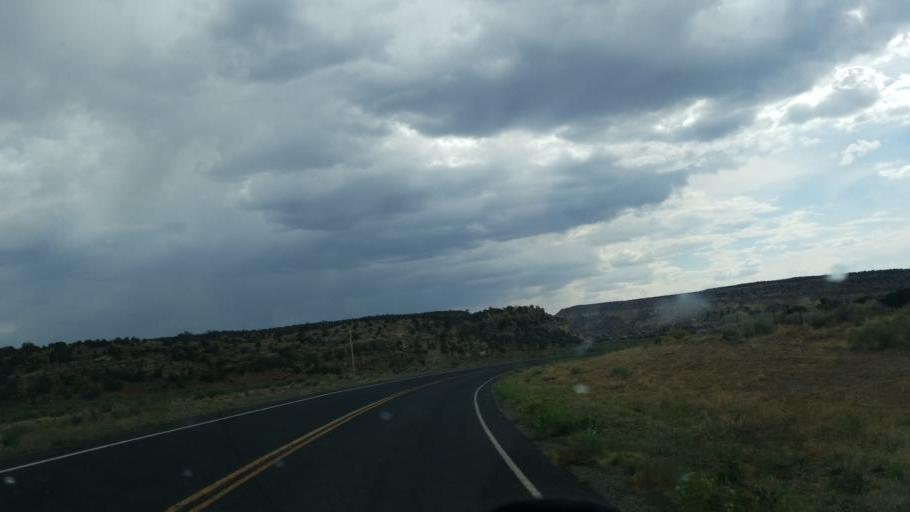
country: US
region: Arizona
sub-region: Apache County
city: Saint Michaels
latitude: 35.4161
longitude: -108.9824
